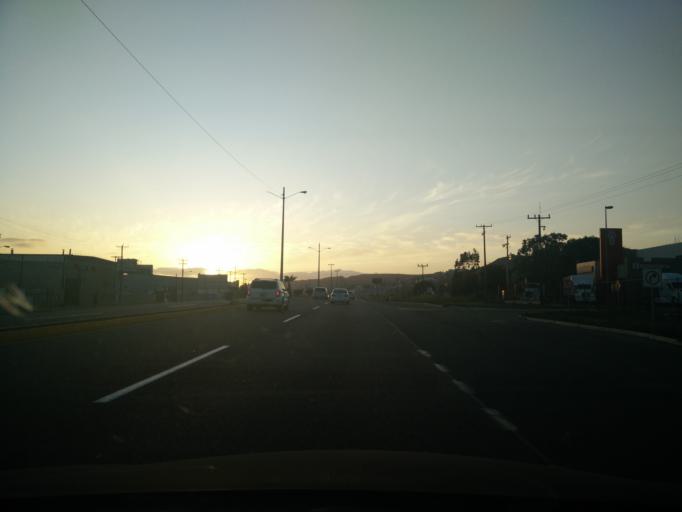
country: MX
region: Baja California
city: El Sauzal
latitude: 31.8998
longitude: -116.7071
